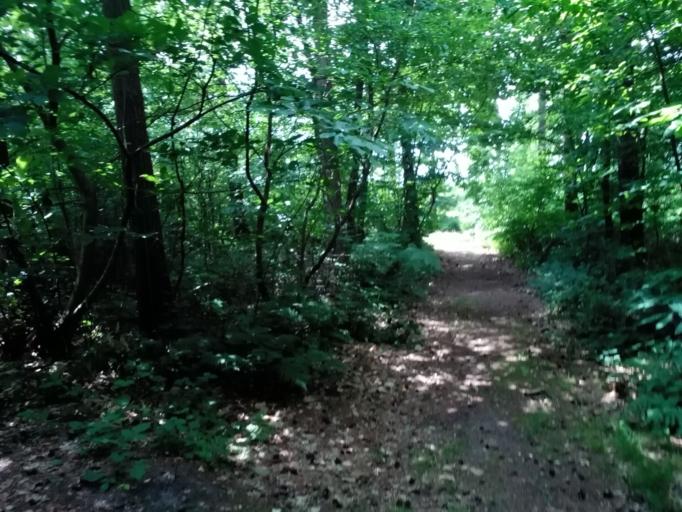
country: BE
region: Flanders
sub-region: Provincie Vlaams-Brabant
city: Oud-Heverlee
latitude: 50.7968
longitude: 4.6609
